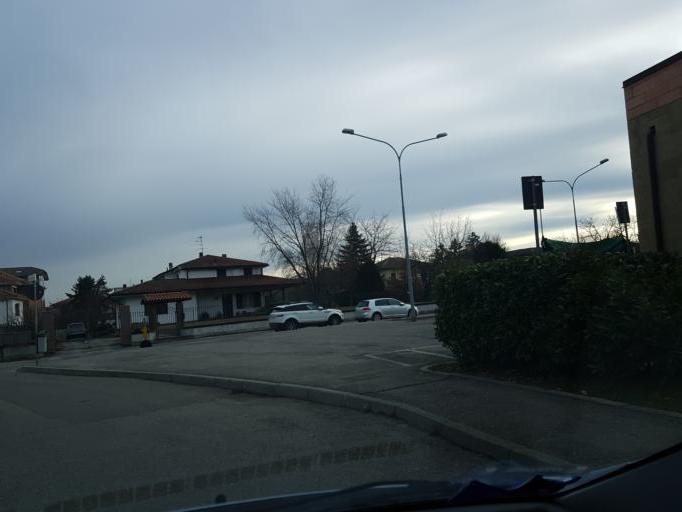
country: IT
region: Piedmont
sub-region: Provincia di Alessandria
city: Novi Ligure
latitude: 44.7630
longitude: 8.8015
